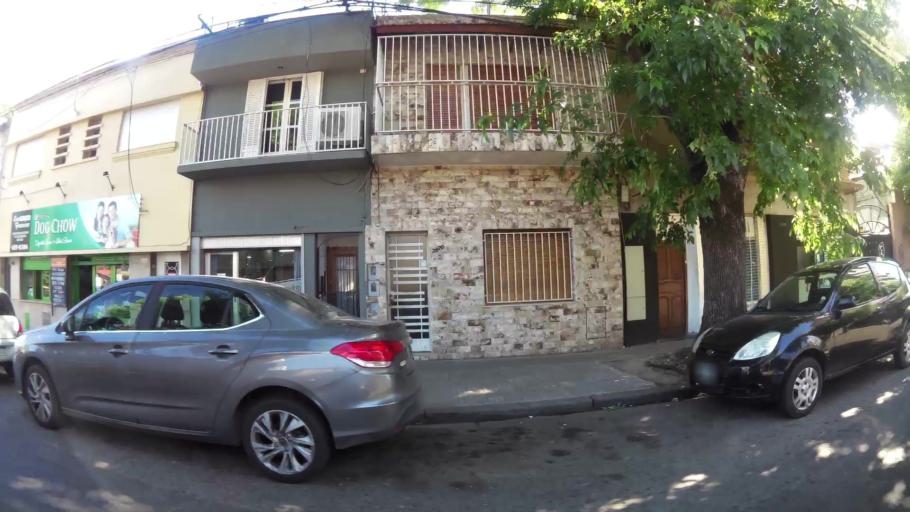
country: AR
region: Santa Fe
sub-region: Departamento de Rosario
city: Rosario
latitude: -32.9434
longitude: -60.6770
